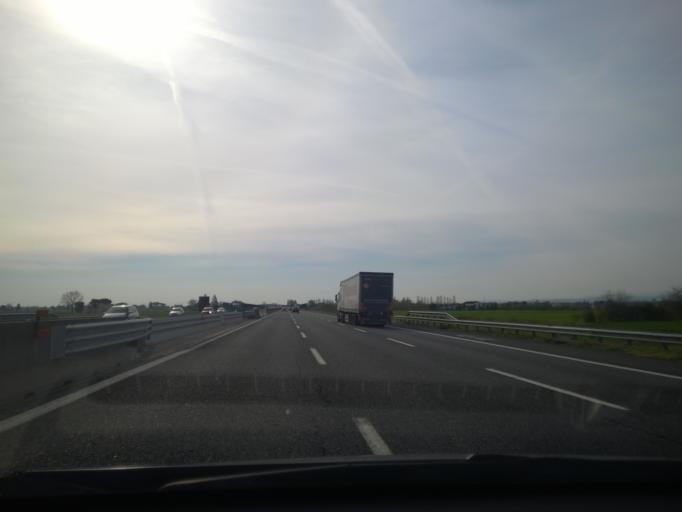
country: IT
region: Emilia-Romagna
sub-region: Forli-Cesena
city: Santa Maria Nuova
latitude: 44.2129
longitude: 12.1839
